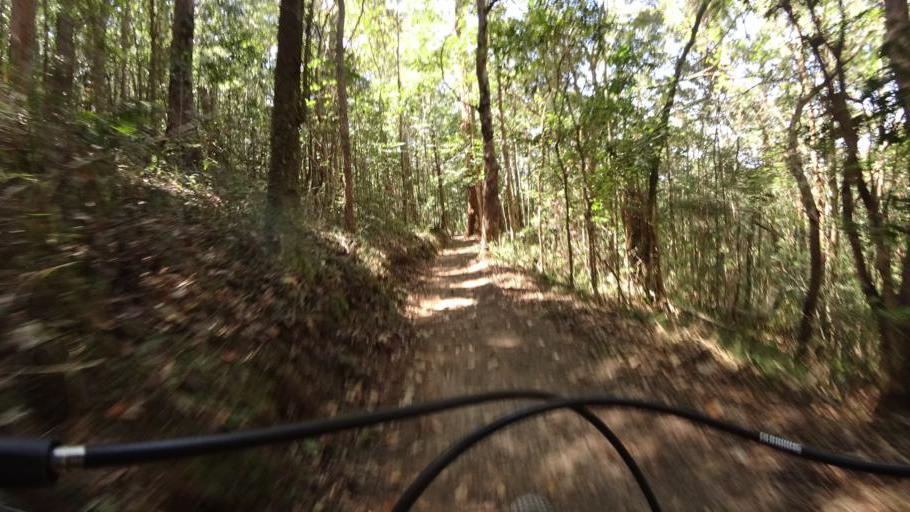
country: AU
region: Queensland
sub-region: Moreton Bay
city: Highvale
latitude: -27.4058
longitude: 152.8078
